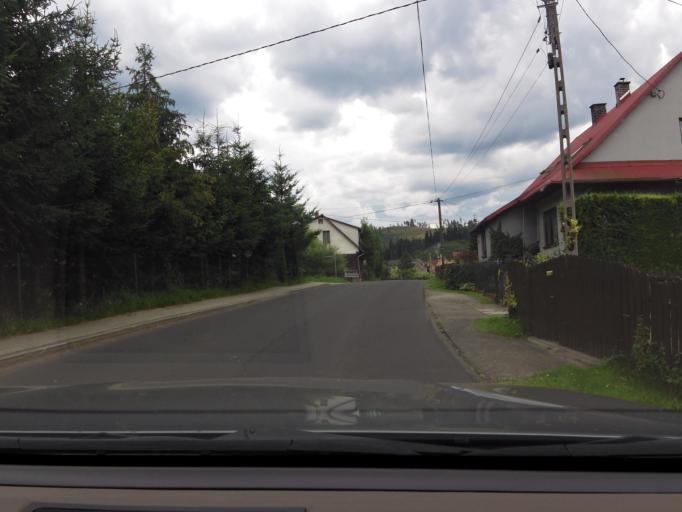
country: PL
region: Silesian Voivodeship
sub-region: Powiat zywiecki
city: Ujsoly
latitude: 49.4726
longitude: 19.1499
